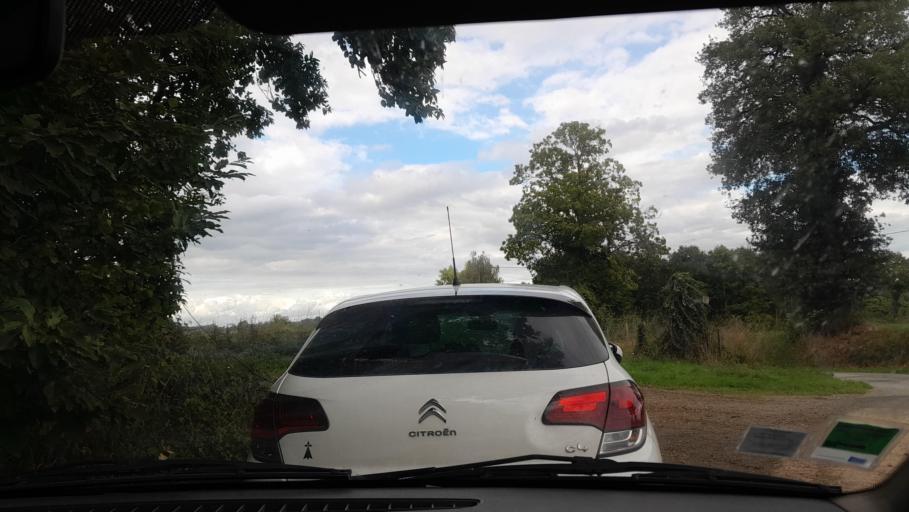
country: FR
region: Brittany
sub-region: Departement d'Ille-et-Vilaine
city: Argentre-du-Plessis
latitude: 48.0577
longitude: -1.1259
